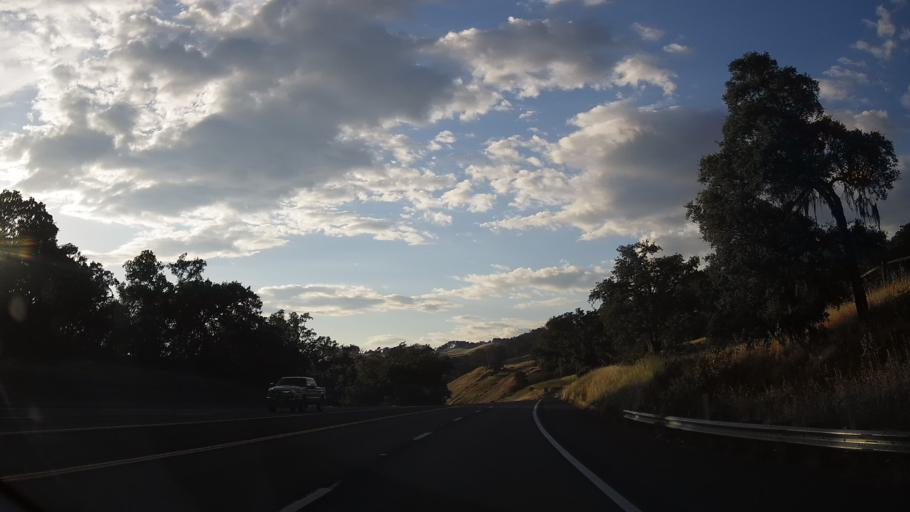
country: US
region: California
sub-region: Sonoma County
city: Cloverdale
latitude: 38.9331
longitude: -123.0619
